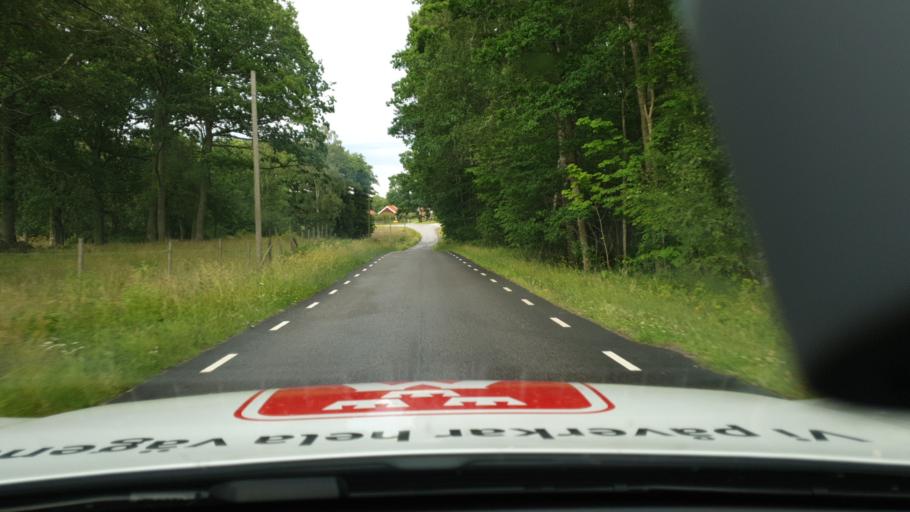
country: SE
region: Vaestra Goetaland
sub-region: Mariestads Kommun
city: Mariestad
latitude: 58.6158
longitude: 13.7311
